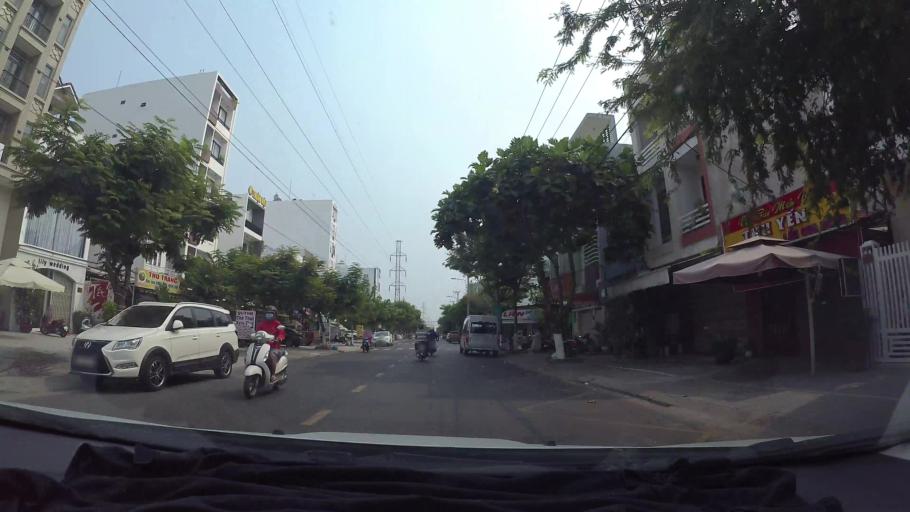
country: VN
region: Da Nang
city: Son Tra
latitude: 16.0435
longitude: 108.2180
